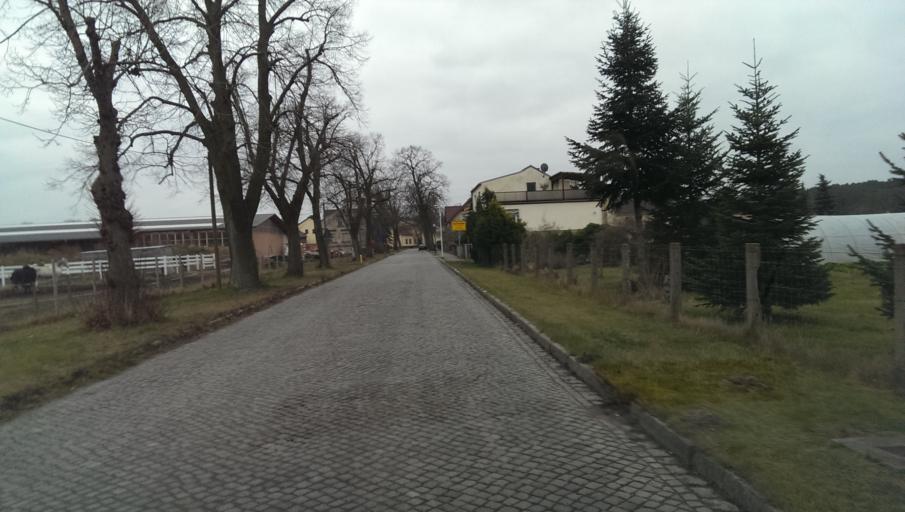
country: DE
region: Brandenburg
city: Mittenwalde
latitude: 52.2145
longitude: 13.5560
